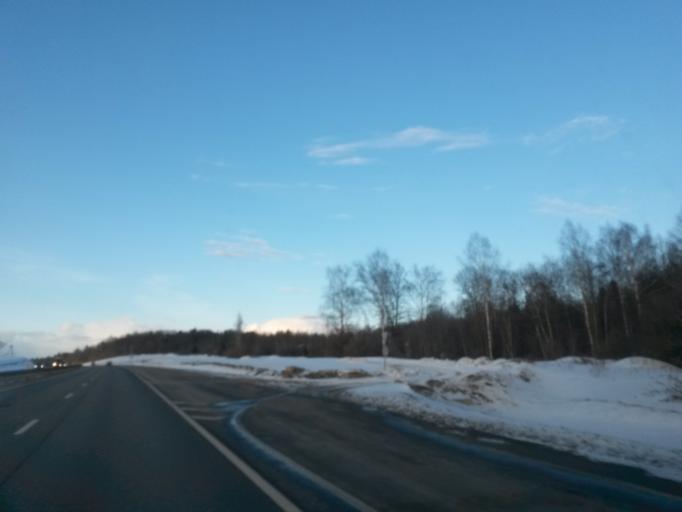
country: RU
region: Moskovskaya
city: Krasnozavodsk
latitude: 56.4271
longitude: 38.3397
